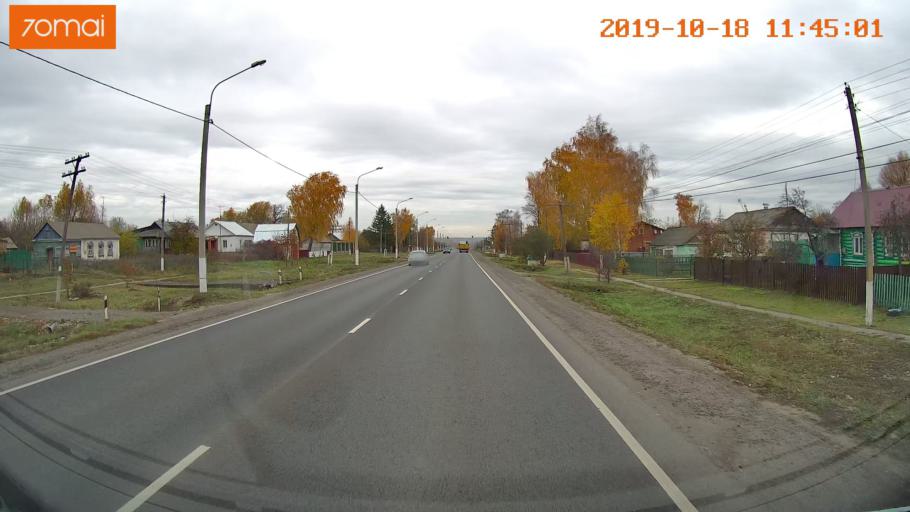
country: RU
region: Rjazan
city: Mikhaylov
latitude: 54.2070
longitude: 38.9650
